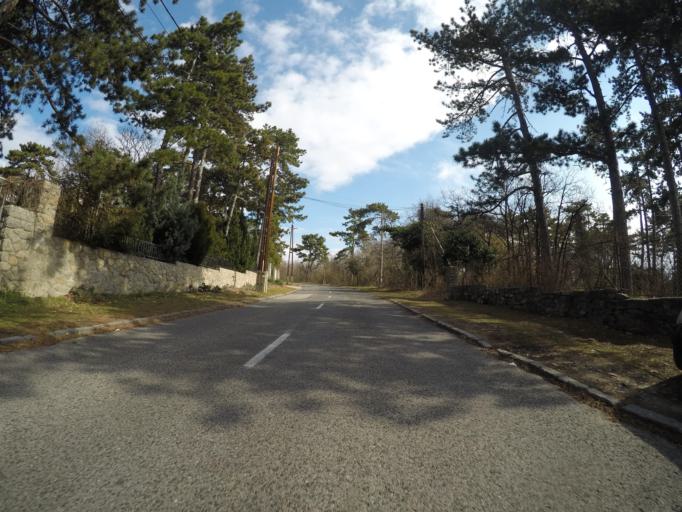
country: HU
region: Baranya
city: Pecs
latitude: 46.0892
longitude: 18.2279
